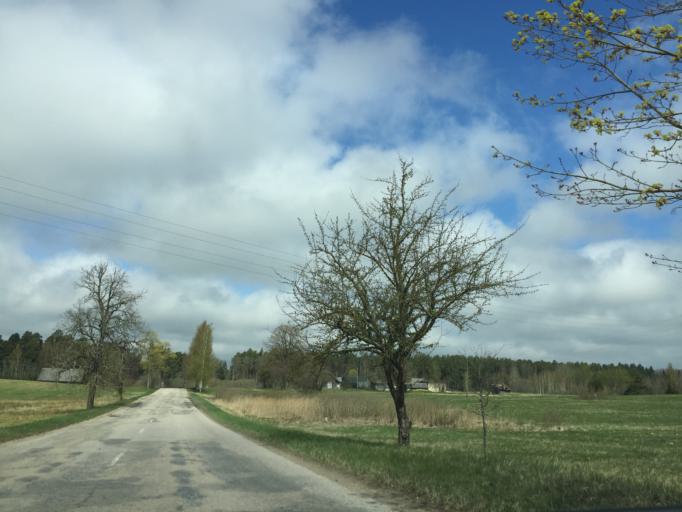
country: LV
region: Apes Novads
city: Ape
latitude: 57.5002
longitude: 26.4020
